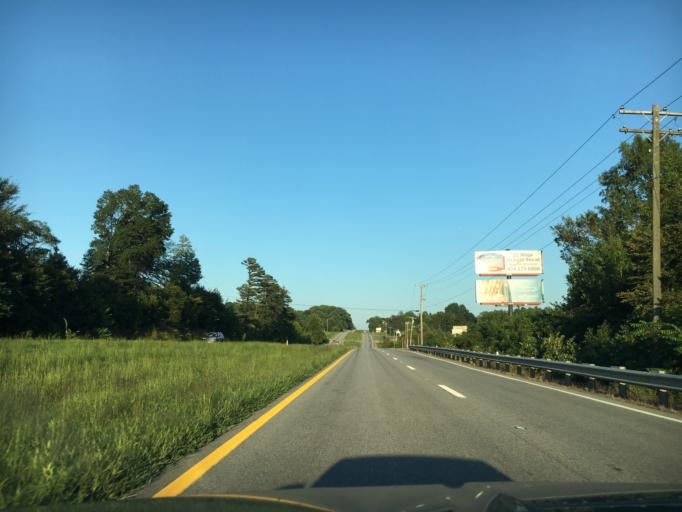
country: US
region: Virginia
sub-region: City of Danville
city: Danville
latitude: 36.5807
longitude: -79.2923
